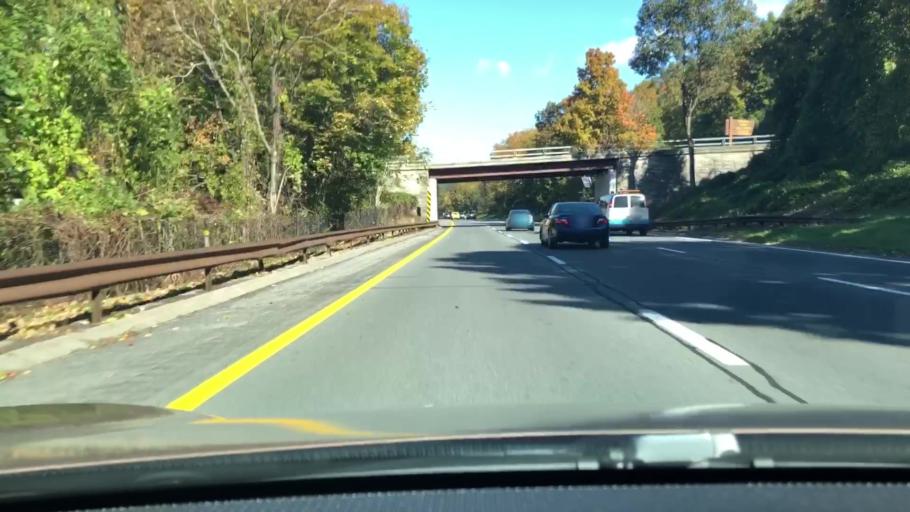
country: US
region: New York
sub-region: Westchester County
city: Greenville
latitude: 40.9796
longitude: -73.8409
